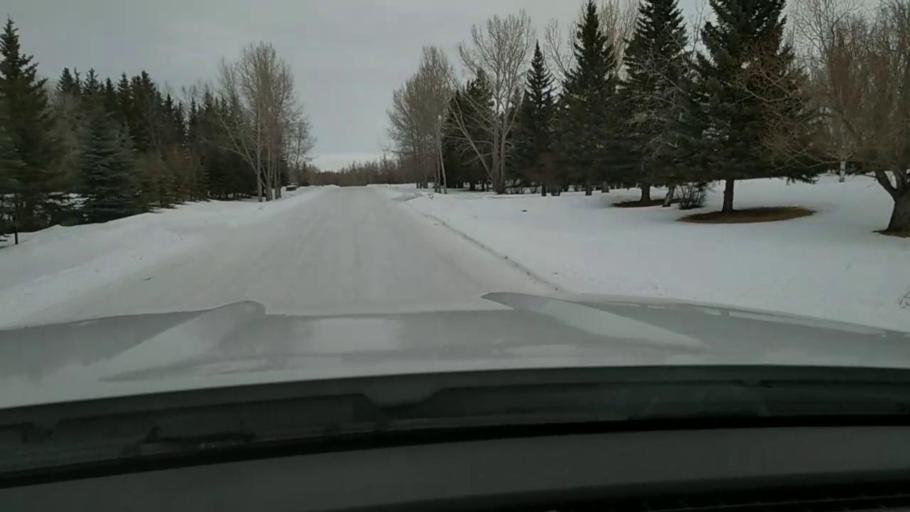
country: CA
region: Alberta
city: Calgary
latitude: 51.1171
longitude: -114.2668
